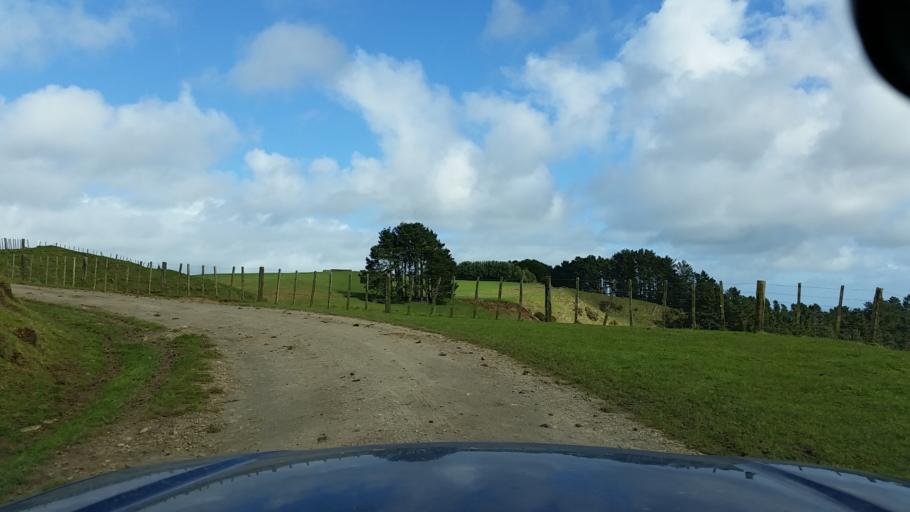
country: NZ
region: Taranaki
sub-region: South Taranaki District
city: Patea
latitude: -39.6577
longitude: 174.5695
